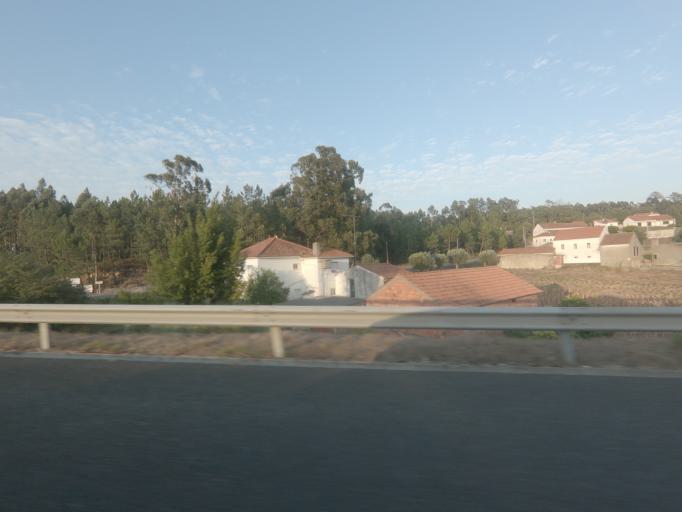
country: PT
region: Leiria
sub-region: Leiria
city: Caranguejeira
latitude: 39.7180
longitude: -8.7133
